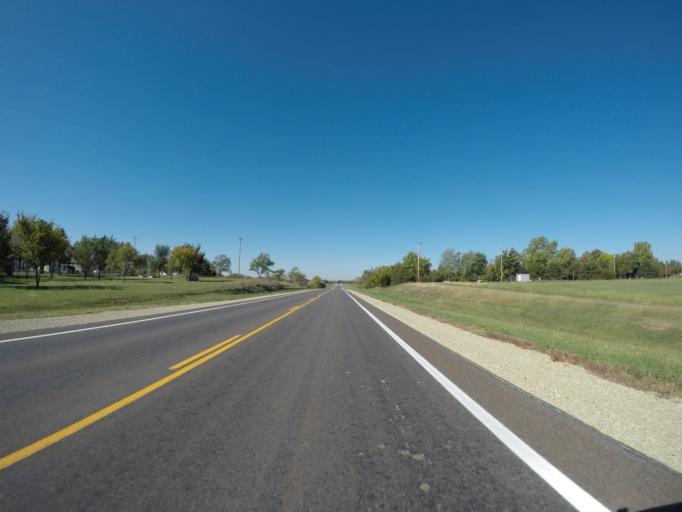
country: US
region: Kansas
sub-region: Riley County
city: Fort Riley North
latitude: 39.3036
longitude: -96.8240
